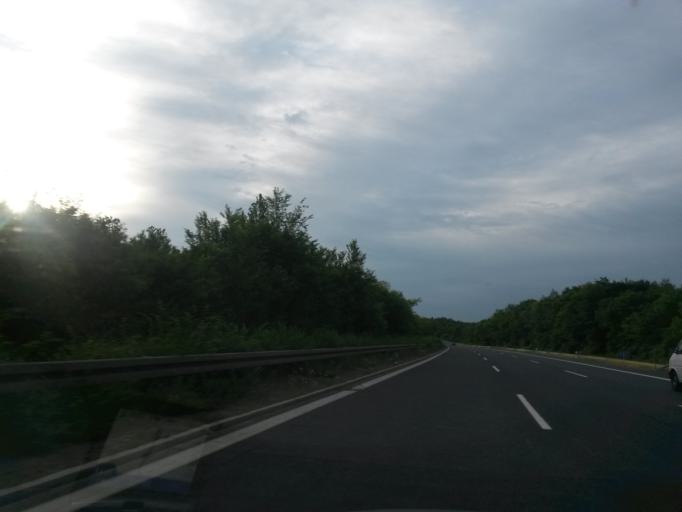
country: DE
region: Bavaria
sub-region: Regierungsbezirk Mittelfranken
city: Wendelstein
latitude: 49.3685
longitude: 11.1714
